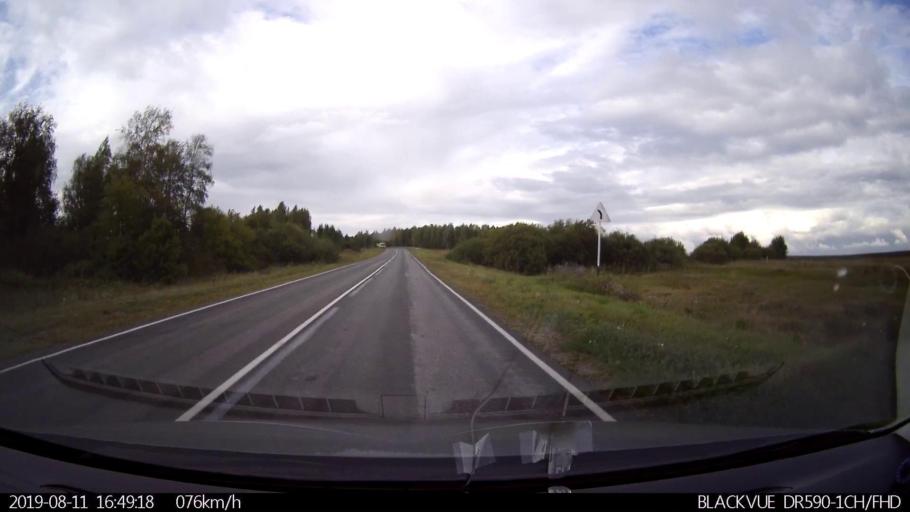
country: RU
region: Ulyanovsk
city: Mayna
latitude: 54.2195
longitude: 47.6954
